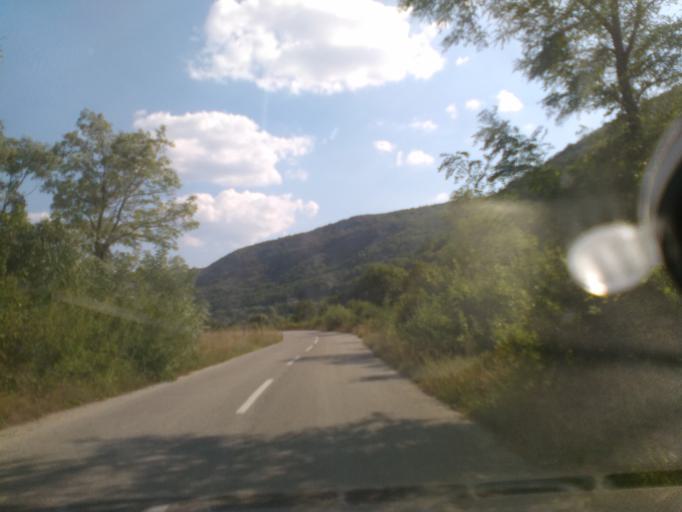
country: BA
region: Federation of Bosnia and Herzegovina
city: Orasac
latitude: 44.4976
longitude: 16.1338
